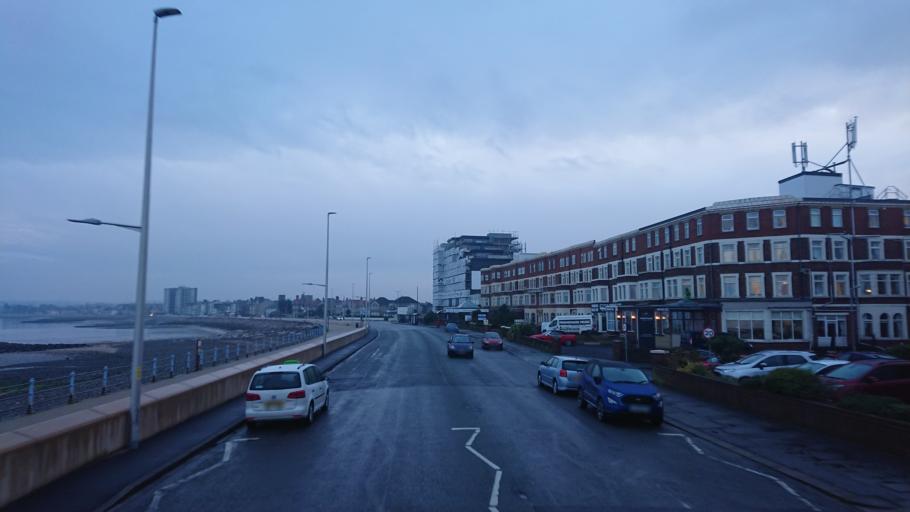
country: GB
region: England
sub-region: Lancashire
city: Morecambe
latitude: 54.0771
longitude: -2.8517
